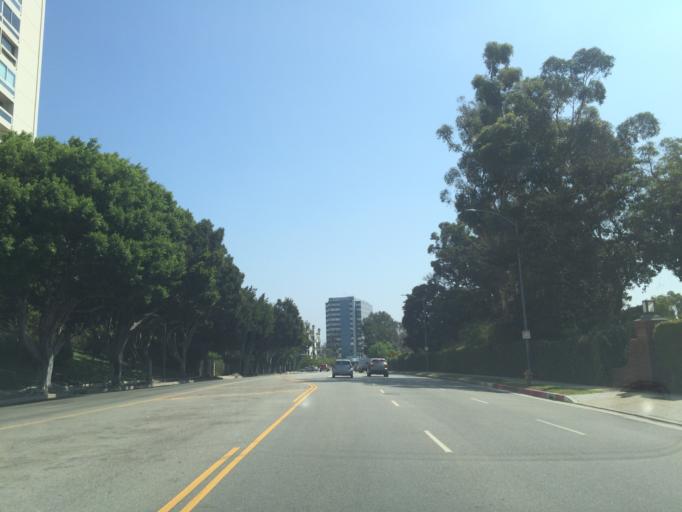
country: US
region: California
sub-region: Los Angeles County
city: Century City
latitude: 34.0514
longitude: -118.4082
